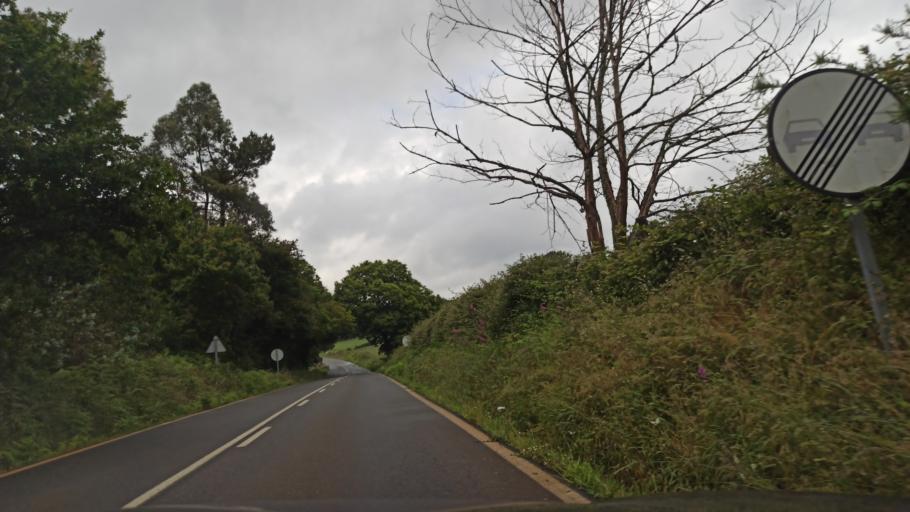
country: ES
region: Galicia
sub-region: Provincia da Coruna
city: Santiso
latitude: 42.7789
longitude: -8.0369
